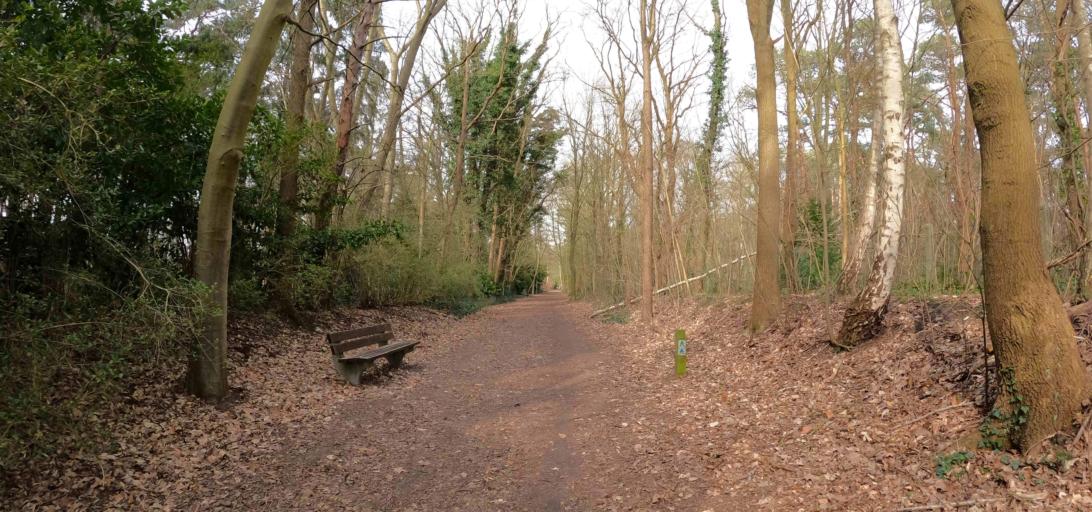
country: BE
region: Flanders
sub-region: Provincie Oost-Vlaanderen
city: Waasmunster
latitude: 51.1232
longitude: 4.0904
